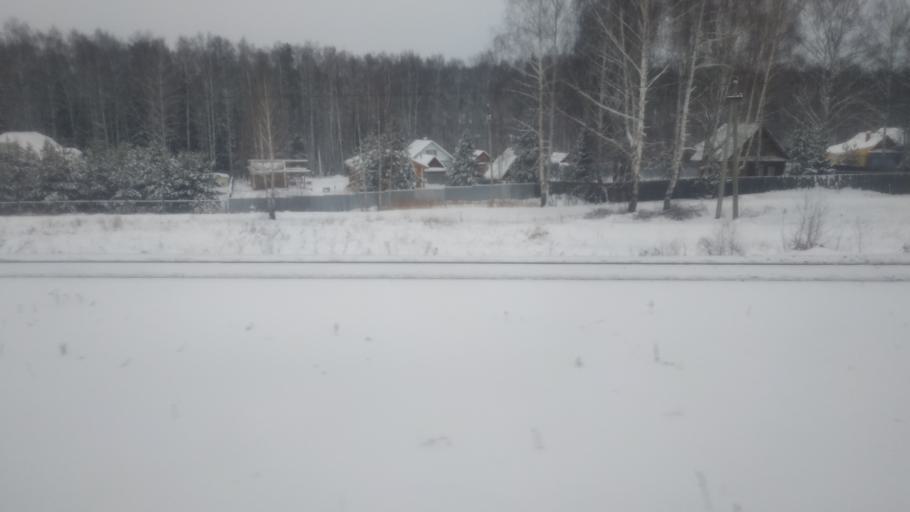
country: RU
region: Udmurtiya
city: Malaya Purga
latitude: 56.5547
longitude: 53.1095
